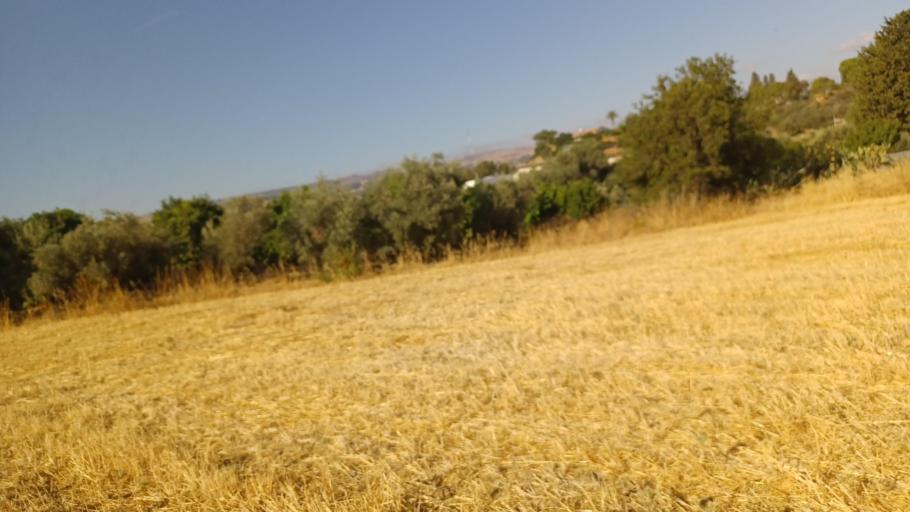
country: CY
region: Pafos
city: Polis
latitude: 35.0319
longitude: 32.4330
